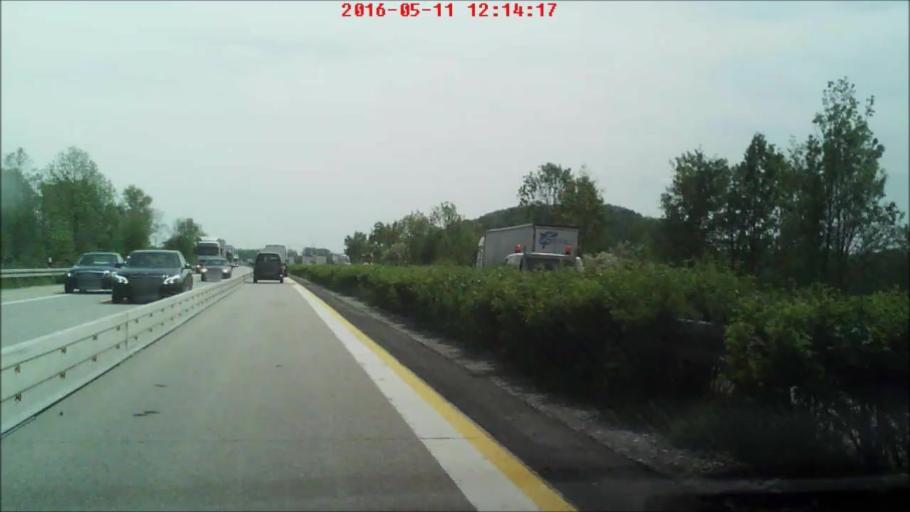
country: DE
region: Bavaria
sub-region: Lower Bavaria
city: Metten
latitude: 48.8362
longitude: 12.9036
